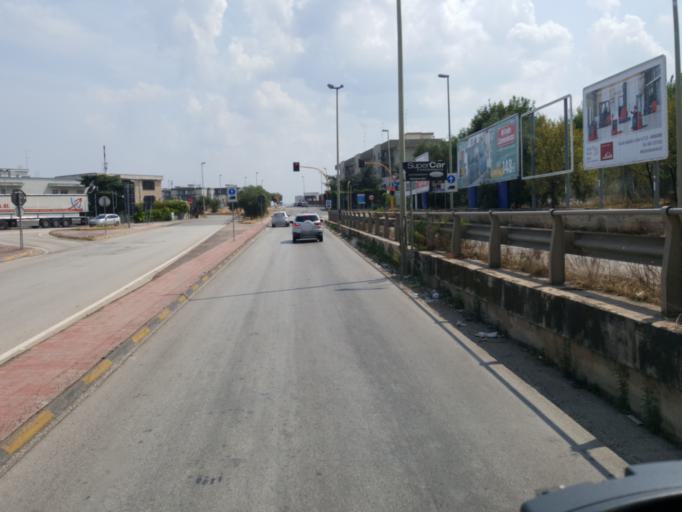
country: IT
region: Apulia
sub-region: Provincia di Bari
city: Modugno
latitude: 41.0912
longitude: 16.7774
